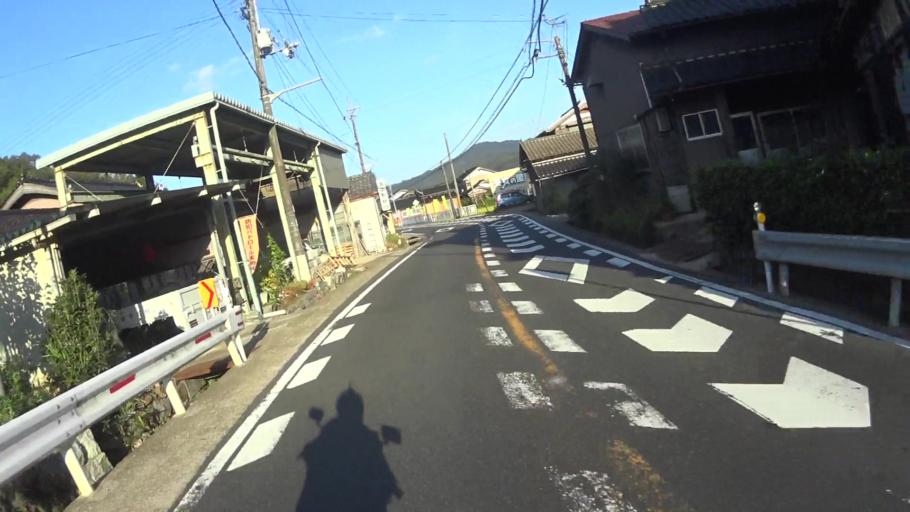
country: JP
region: Kyoto
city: Miyazu
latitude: 35.5799
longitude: 135.0222
